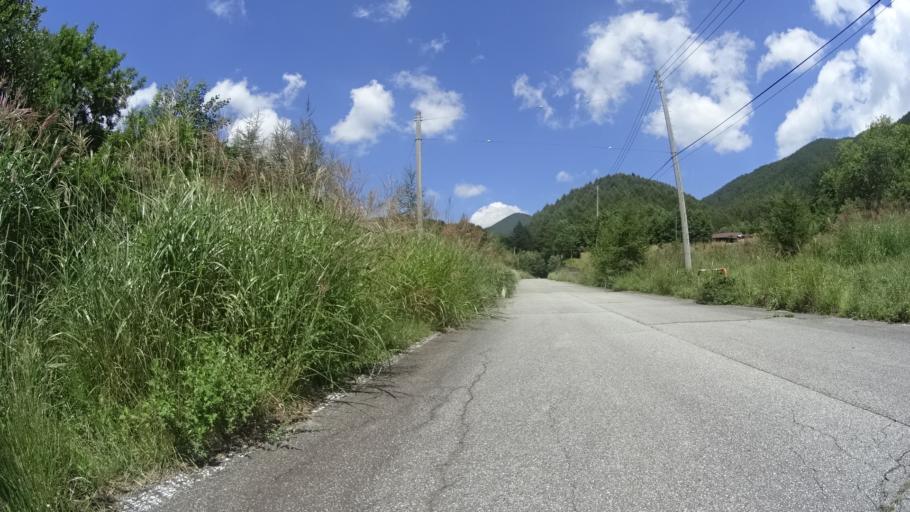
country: JP
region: Yamanashi
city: Enzan
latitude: 35.8132
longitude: 138.6547
